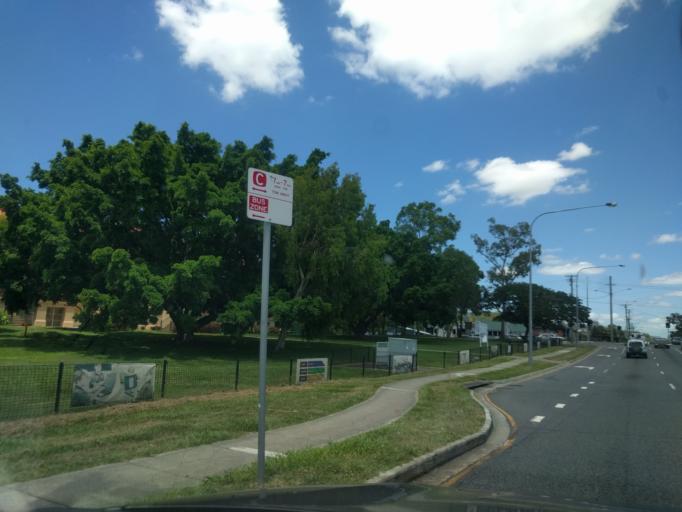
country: AU
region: Queensland
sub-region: Brisbane
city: Stafford
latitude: -27.4107
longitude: 153.0179
